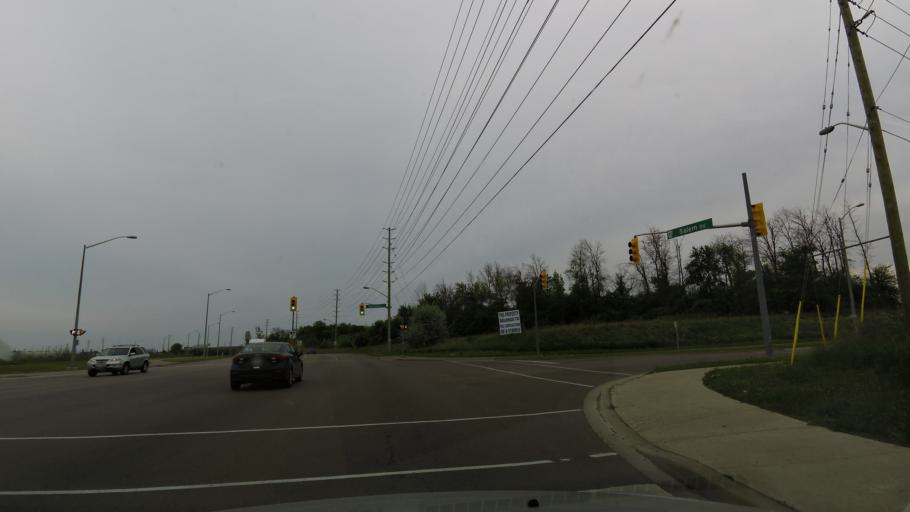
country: CA
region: Ontario
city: Ajax
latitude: 43.8710
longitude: -79.0178
